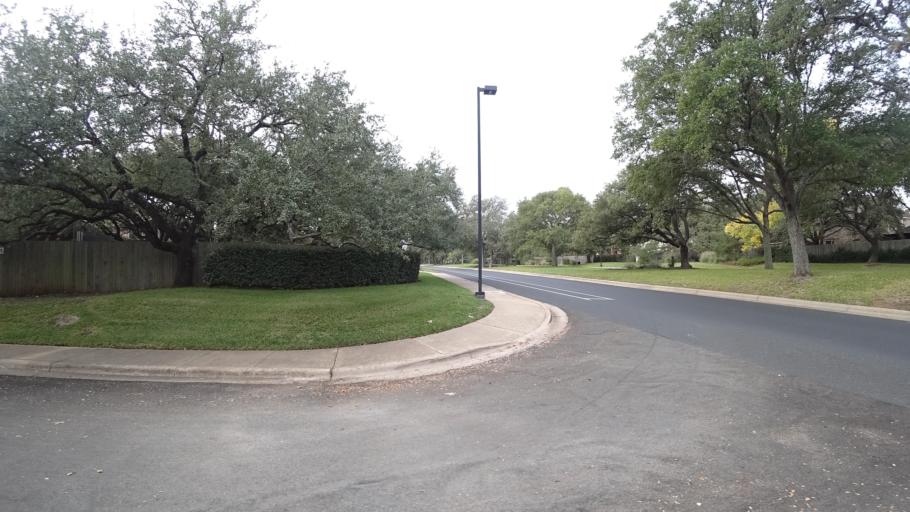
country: US
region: Texas
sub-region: Travis County
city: Shady Hollow
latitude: 30.1923
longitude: -97.8882
